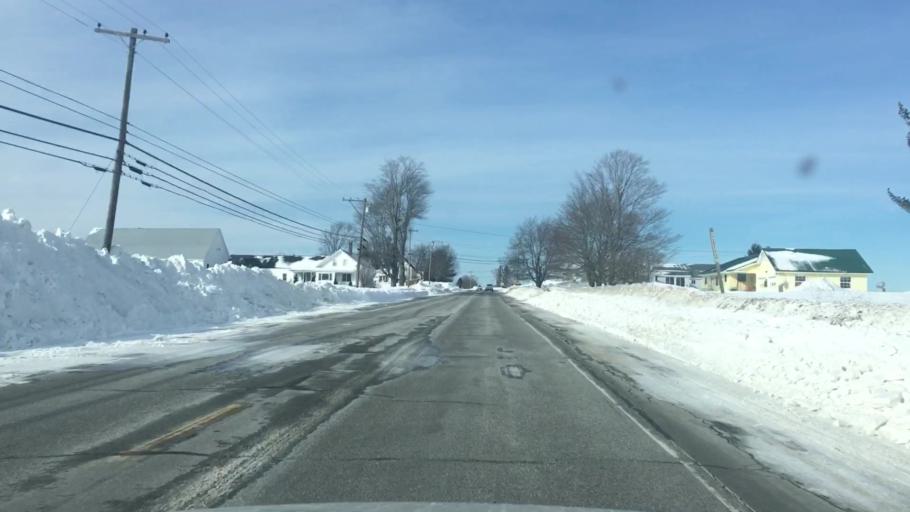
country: US
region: Maine
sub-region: Penobscot County
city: Charleston
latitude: 45.0243
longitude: -69.0298
